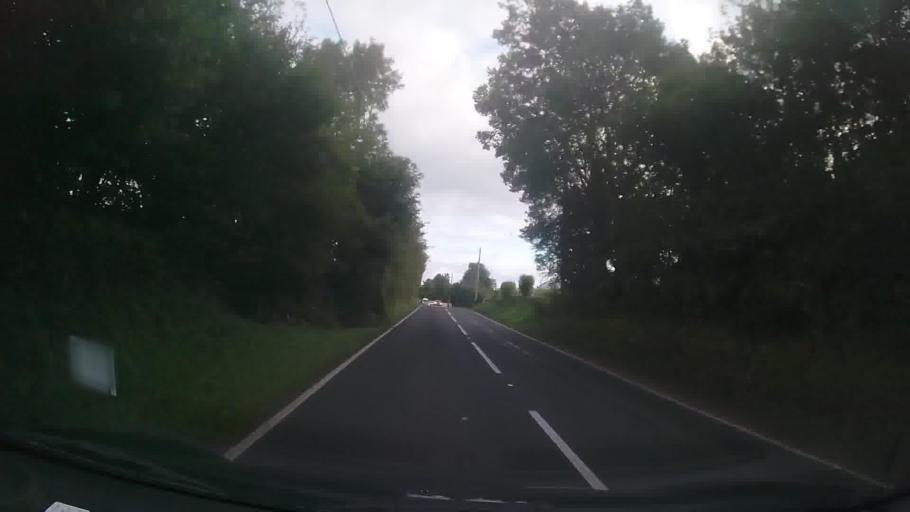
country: GB
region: Wales
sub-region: Pembrokeshire
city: Saundersfoot
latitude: 51.7077
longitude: -4.7262
